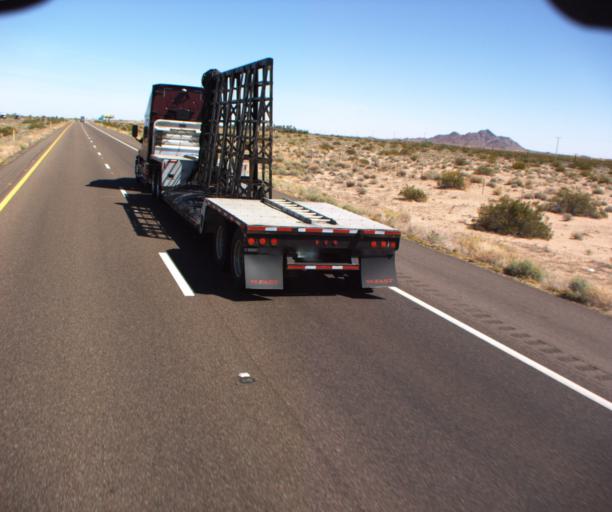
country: US
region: Arizona
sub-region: Yuma County
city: Wellton
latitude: 32.7915
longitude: -113.5561
